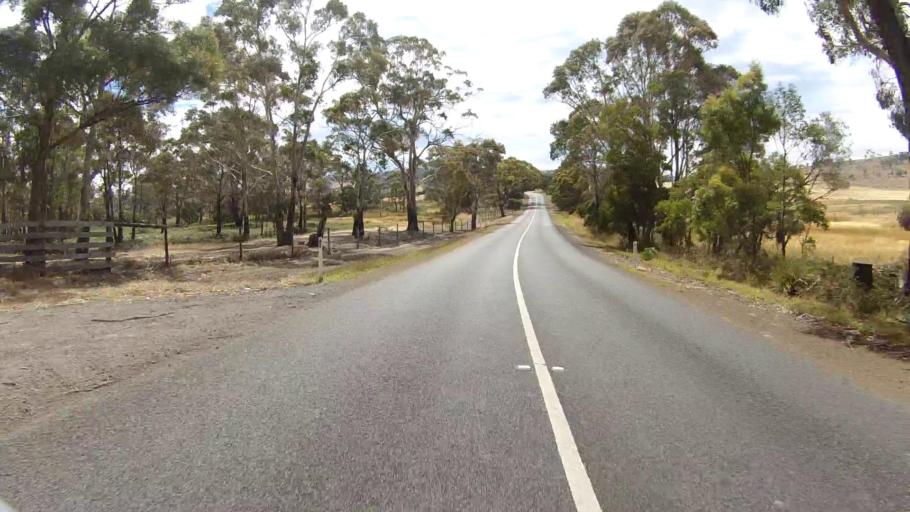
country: AU
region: Tasmania
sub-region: Sorell
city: Sorell
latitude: -42.8771
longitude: 147.6780
